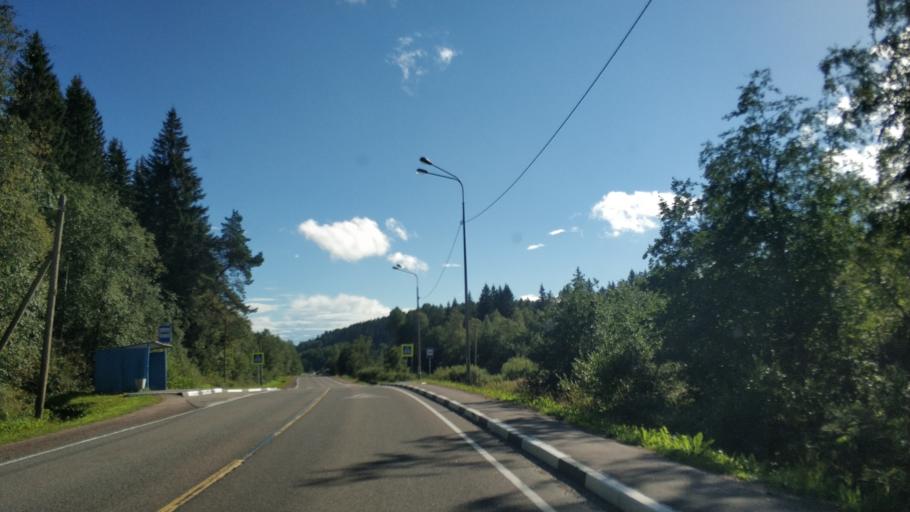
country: RU
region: Republic of Karelia
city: Sortavala
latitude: 61.6727
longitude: 30.6542
